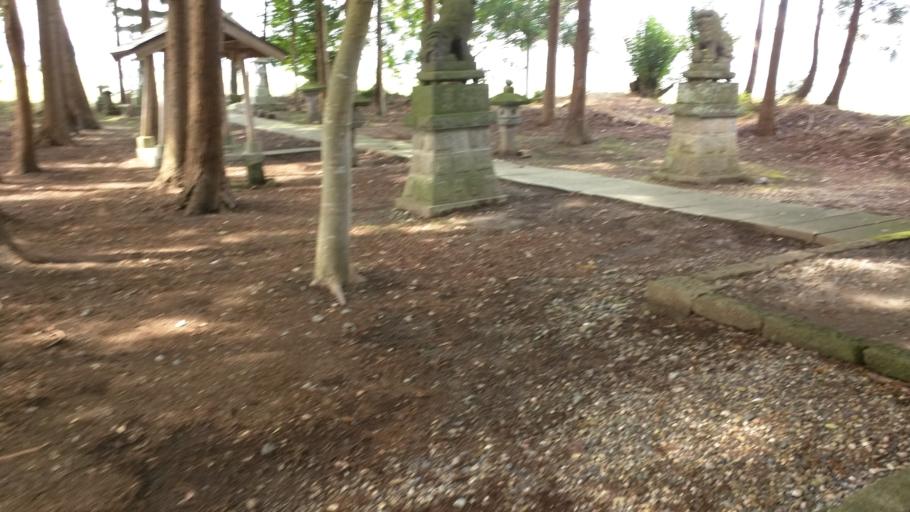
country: JP
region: Fukushima
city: Kitakata
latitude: 37.5373
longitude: 139.8646
